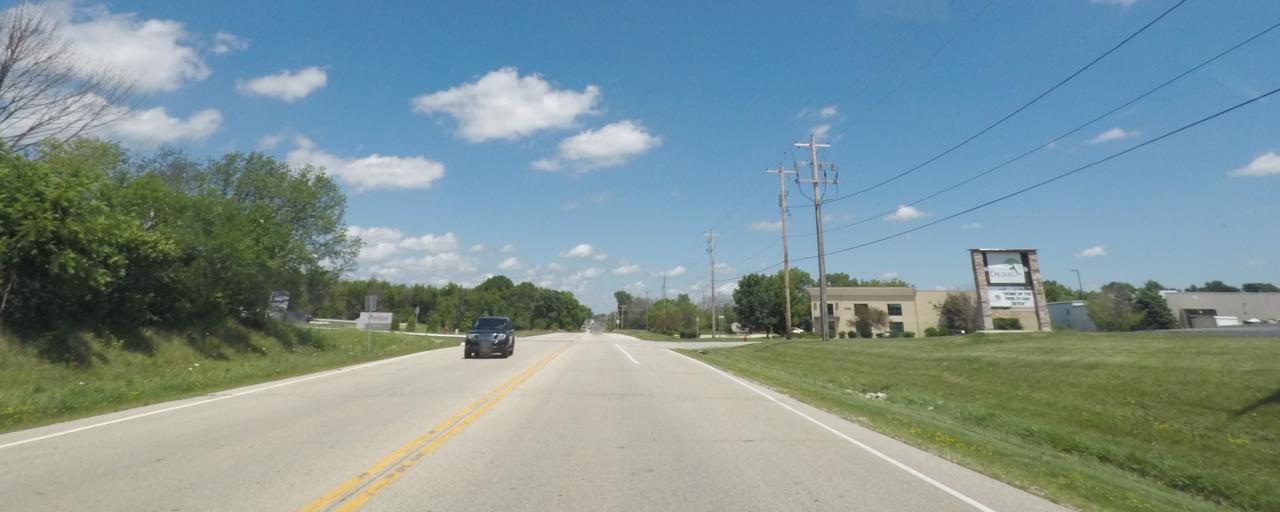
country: US
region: Wisconsin
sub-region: Waukesha County
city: Waukesha
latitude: 43.0427
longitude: -88.1859
